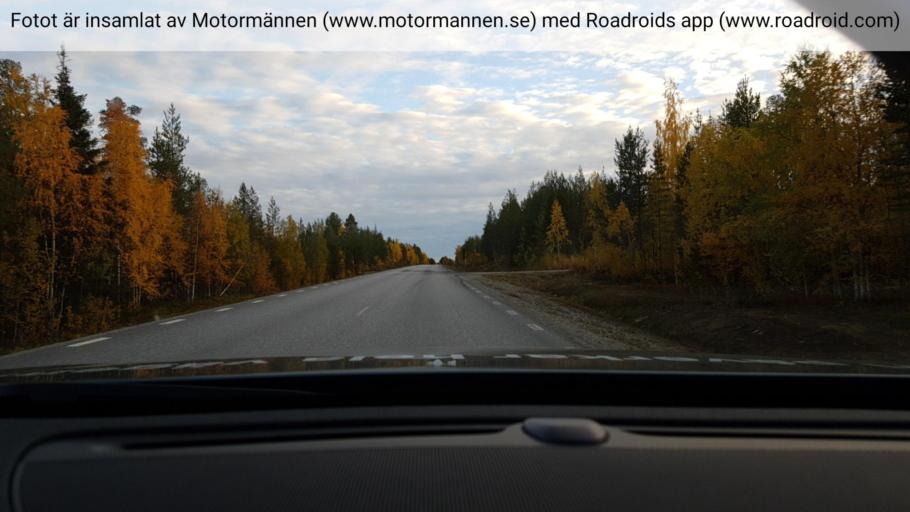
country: SE
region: Norrbotten
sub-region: Jokkmokks Kommun
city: Jokkmokk
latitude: 66.4429
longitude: 19.6944
